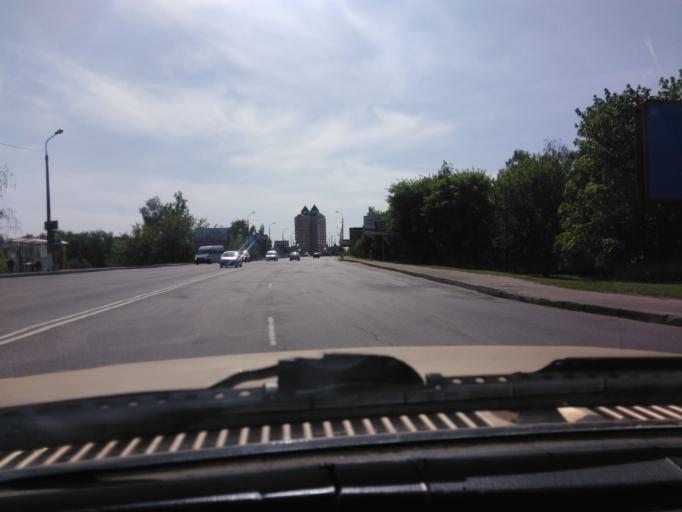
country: BY
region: Mogilev
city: Mahilyow
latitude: 53.9161
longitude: 30.3141
